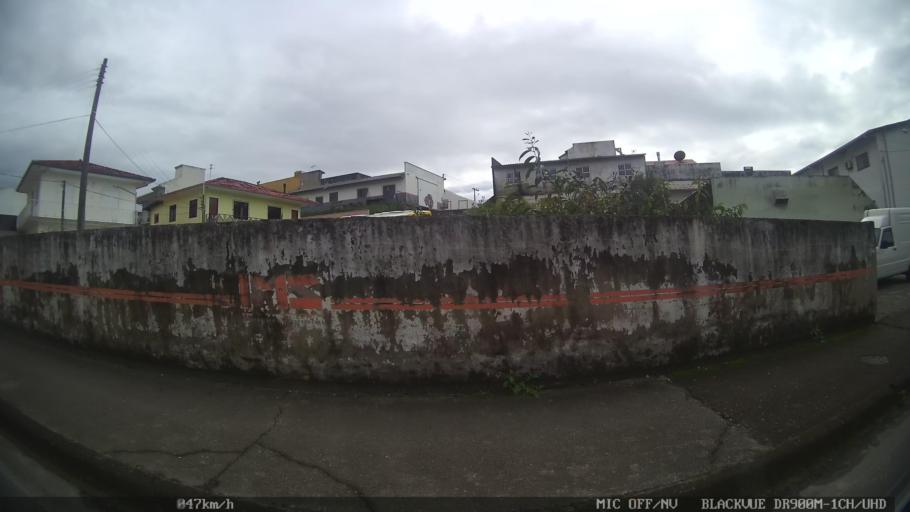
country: BR
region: Santa Catarina
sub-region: Sao Jose
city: Campinas
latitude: -27.5688
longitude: -48.6253
